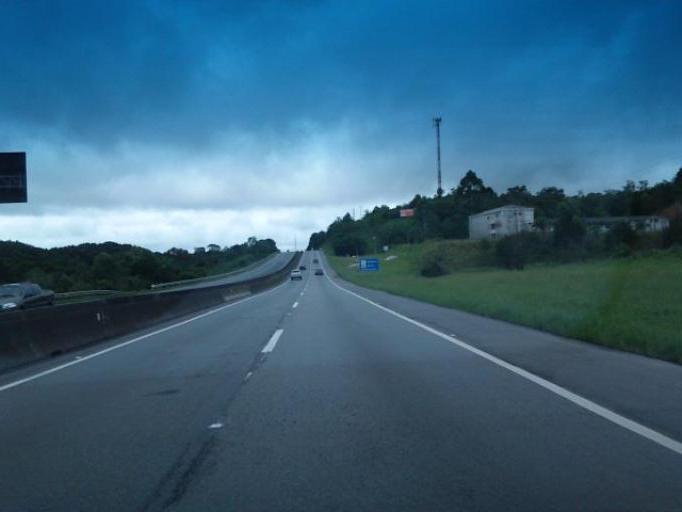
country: BR
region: Parana
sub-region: Campina Grande Do Sul
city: Campina Grande do Sul
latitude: -25.3404
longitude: -49.0396
